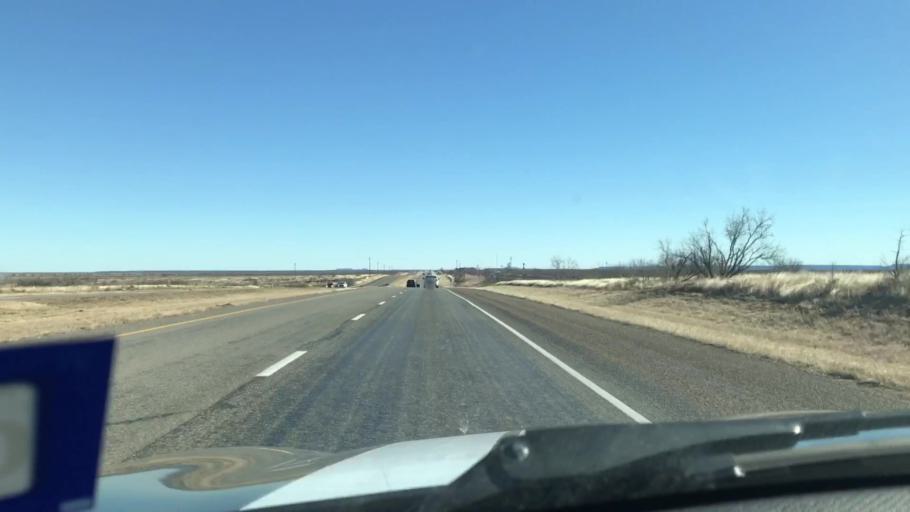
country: US
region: Texas
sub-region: Garza County
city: Post
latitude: 33.1378
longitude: -101.3125
